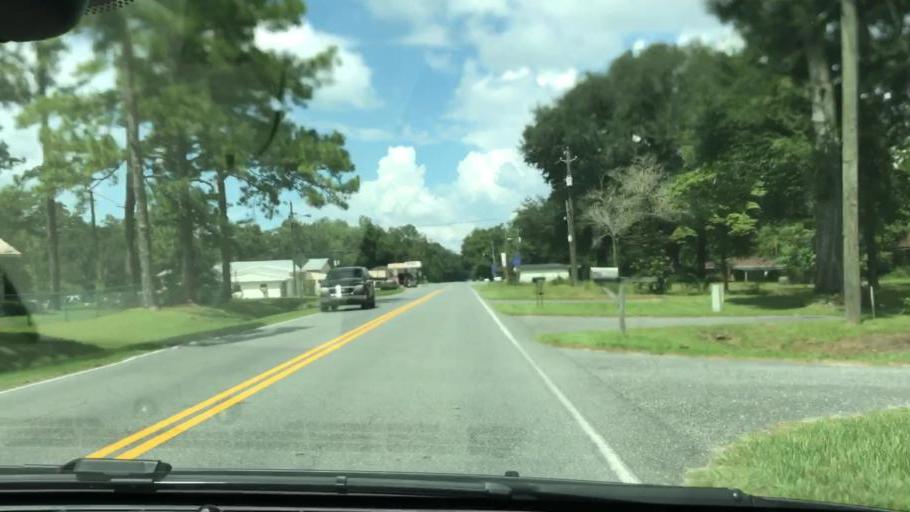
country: US
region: Florida
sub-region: Jackson County
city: Malone
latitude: 30.9249
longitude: -85.1186
